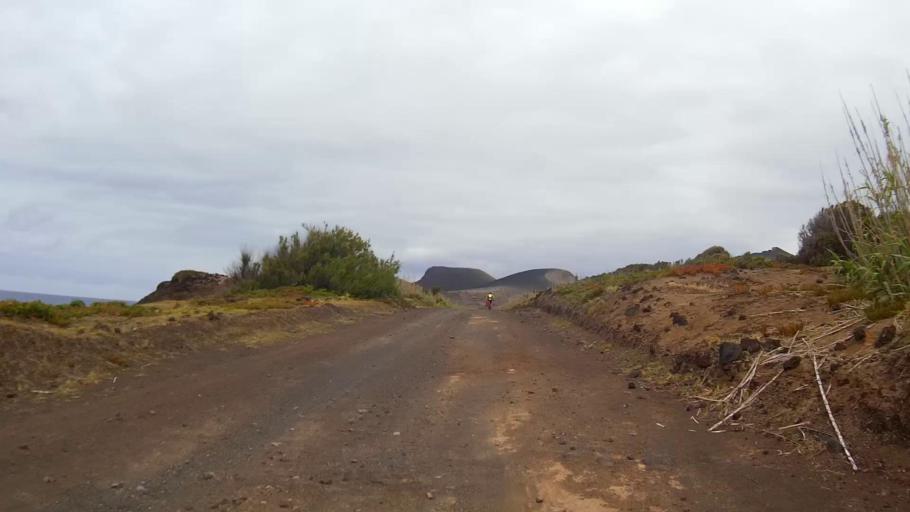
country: PT
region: Azores
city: Ribeira Grande
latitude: 38.5882
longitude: -28.8220
